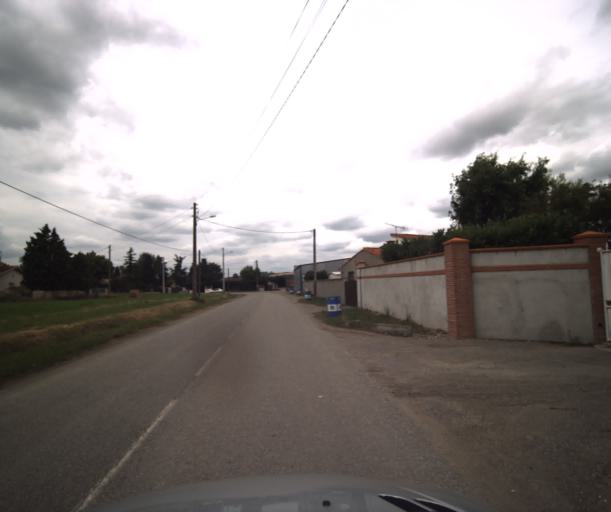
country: FR
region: Midi-Pyrenees
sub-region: Departement de la Haute-Garonne
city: Labarthe-sur-Leze
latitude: 43.4546
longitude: 1.4162
